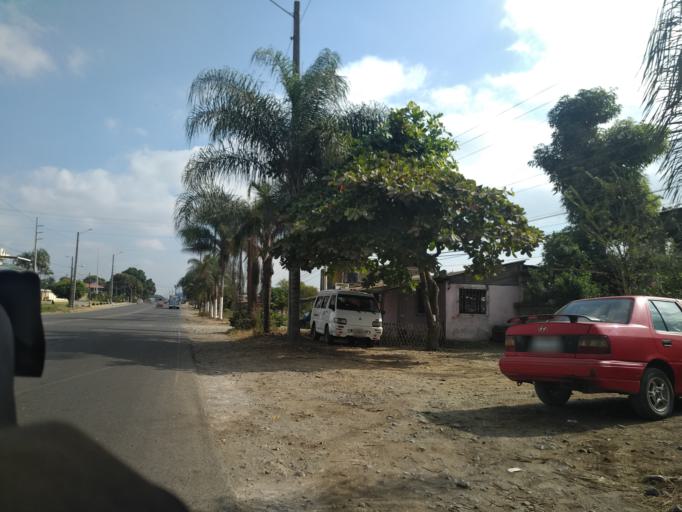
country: EC
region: Los Rios
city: Quevedo
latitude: -1.0577
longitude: -79.4878
